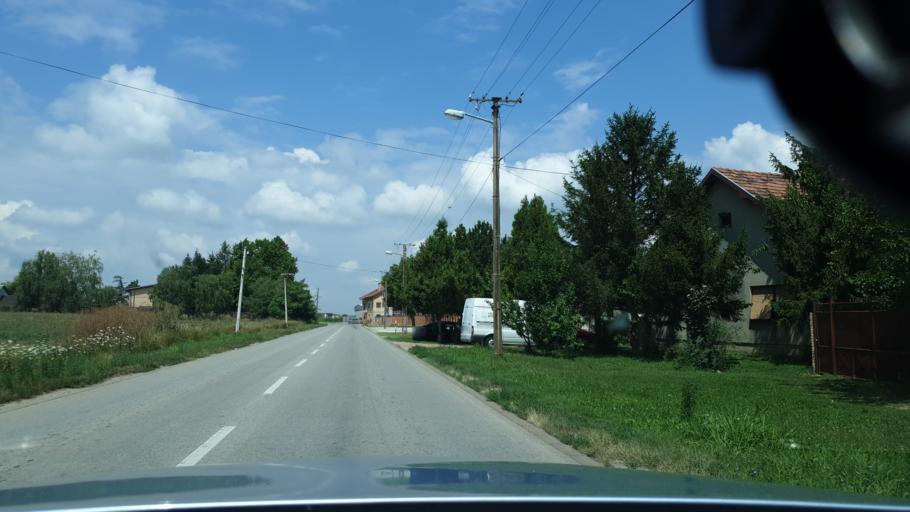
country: RS
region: Autonomna Pokrajina Vojvodina
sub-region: Juznobacki Okrug
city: Kovilj
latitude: 45.2404
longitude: 20.0259
